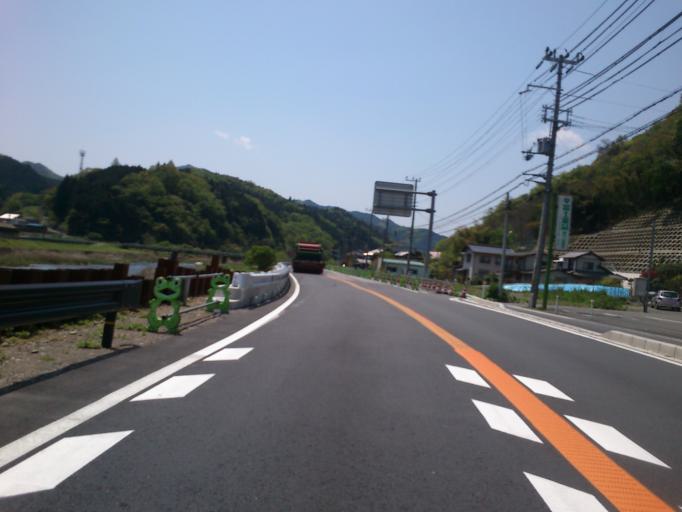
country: JP
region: Kyoto
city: Fukuchiyama
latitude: 35.3322
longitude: 135.0701
